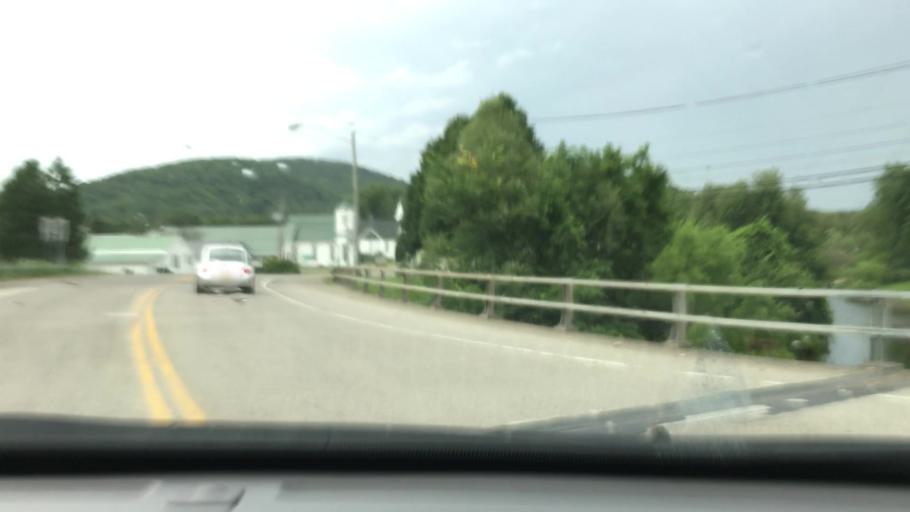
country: US
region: New York
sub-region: Cattaraugus County
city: Salamanca
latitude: 42.2144
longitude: -78.6366
